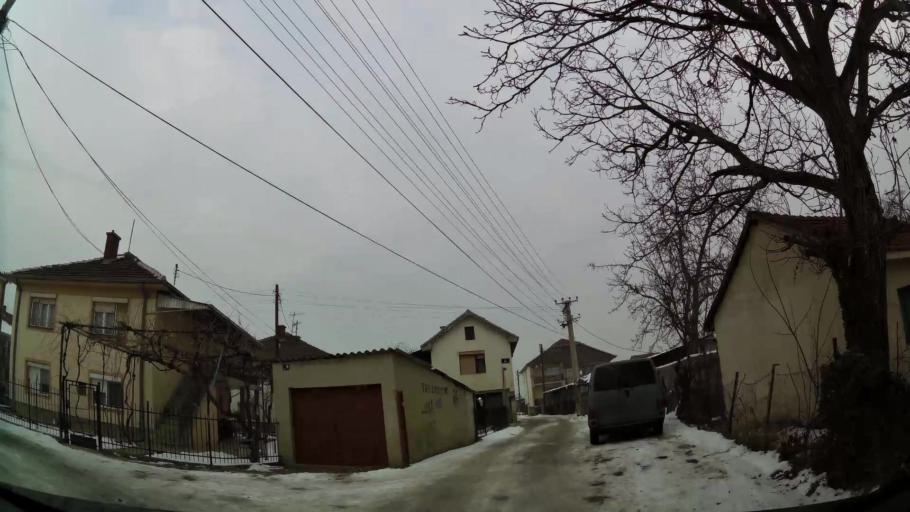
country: MK
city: Kondovo
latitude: 42.0472
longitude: 21.3521
